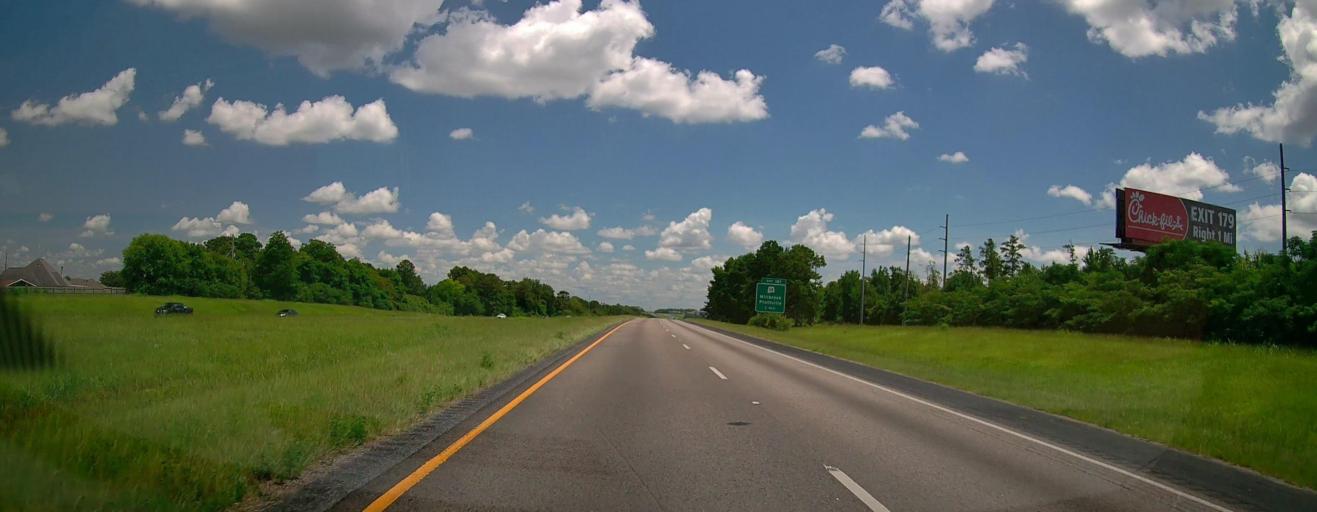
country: US
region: Alabama
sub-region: Autauga County
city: Prattville
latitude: 32.5052
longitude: -86.4211
